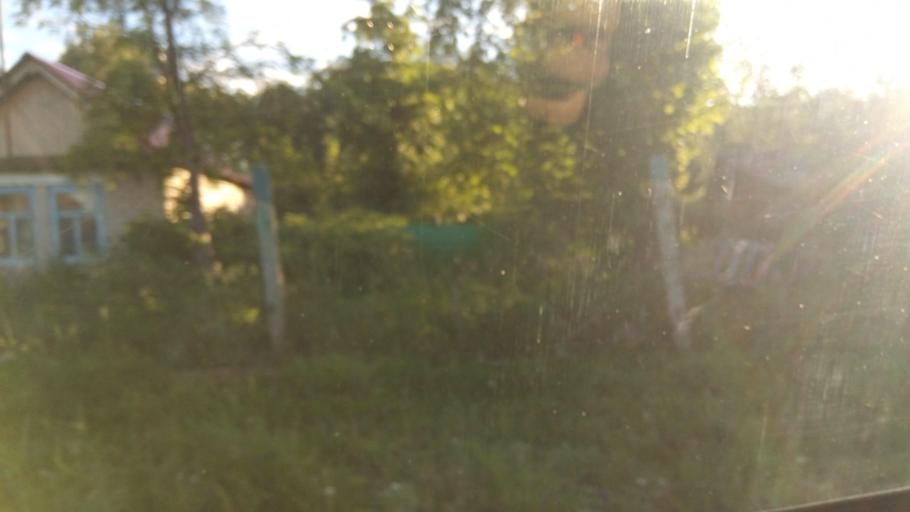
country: RU
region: Chelyabinsk
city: Timiryazevskiy
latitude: 54.9882
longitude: 60.8422
